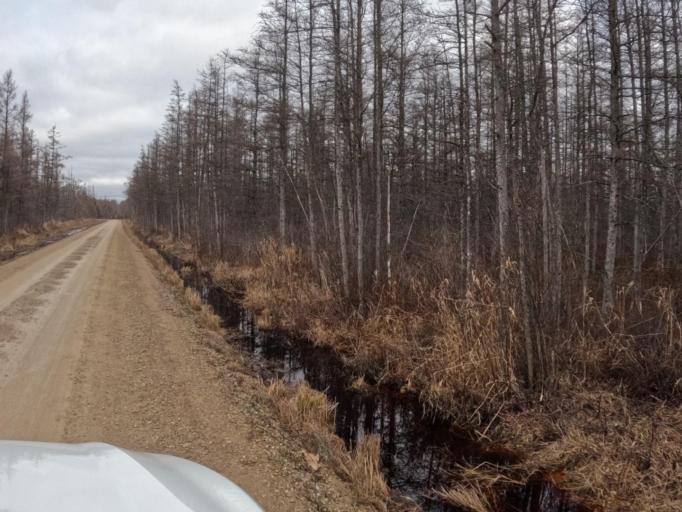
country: CA
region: Ontario
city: Shelburne
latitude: 43.9022
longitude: -80.4091
